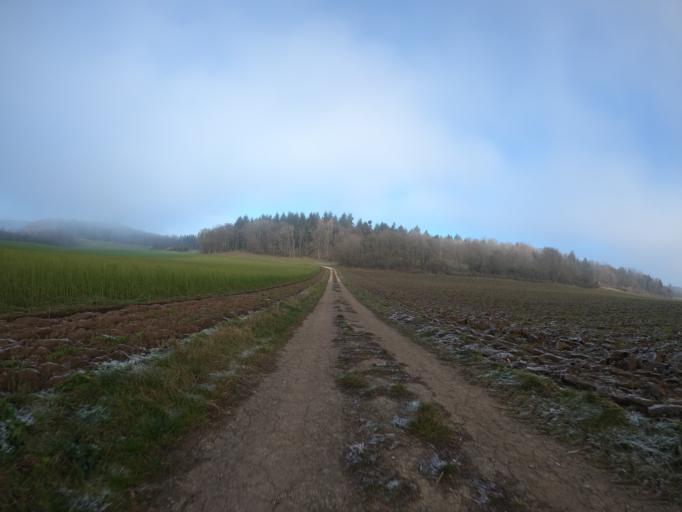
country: DE
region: Baden-Wuerttemberg
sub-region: Regierungsbezirk Stuttgart
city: Deggingen
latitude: 48.5933
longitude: 9.7486
